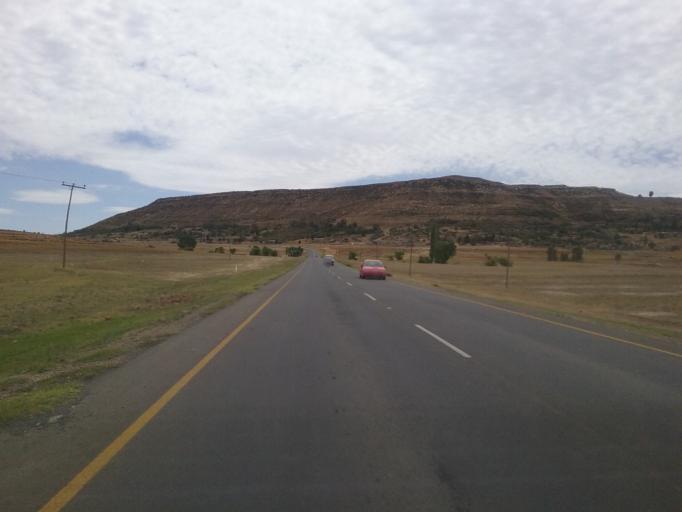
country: LS
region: Maseru
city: Nako
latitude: -29.6143
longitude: 27.4997
